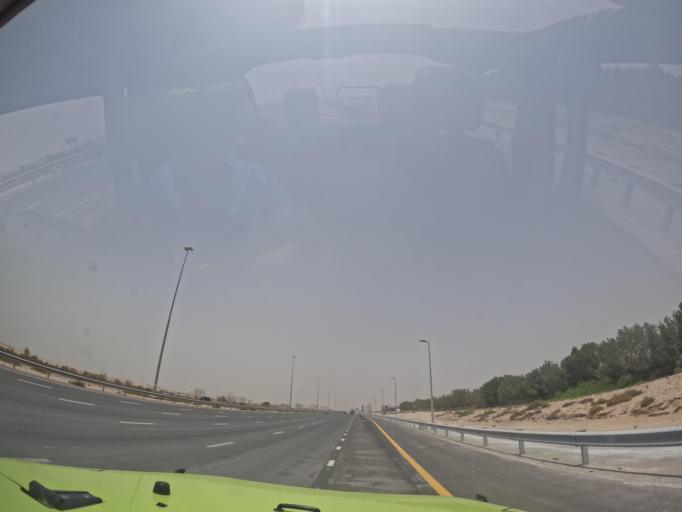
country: AE
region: Dubai
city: Dubai
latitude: 25.0851
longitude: 55.3492
